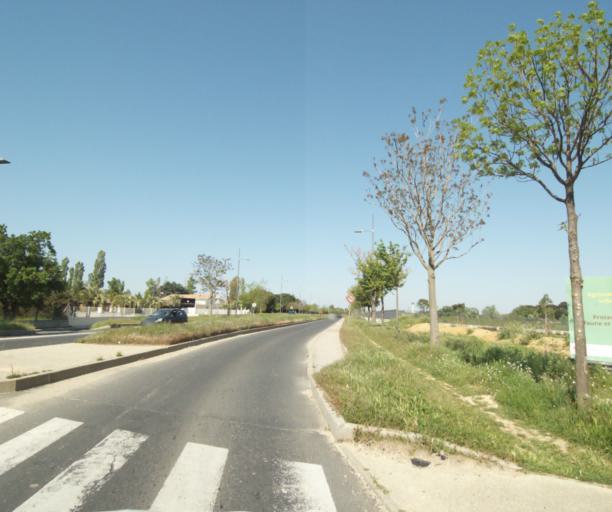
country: FR
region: Languedoc-Roussillon
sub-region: Departement de l'Herault
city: Castelnau-le-Lez
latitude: 43.6223
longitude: 3.9175
